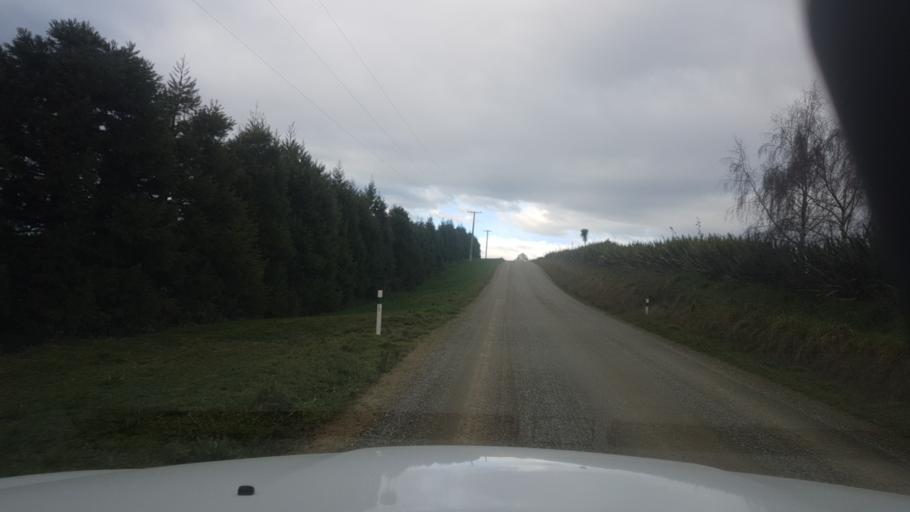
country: NZ
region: Canterbury
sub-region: Timaru District
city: Pleasant Point
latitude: -44.3500
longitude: 171.1559
